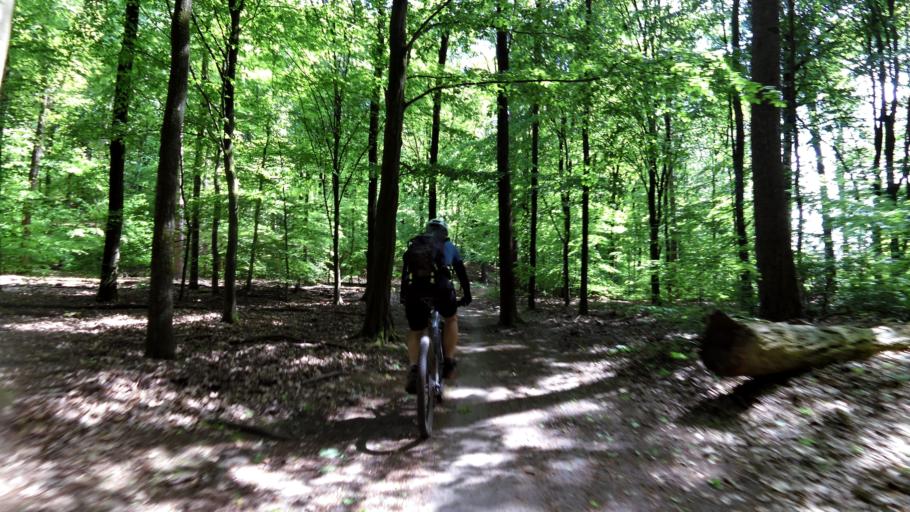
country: NL
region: Gelderland
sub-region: Gemeente Rheden
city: De Steeg
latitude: 52.0188
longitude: 6.0444
